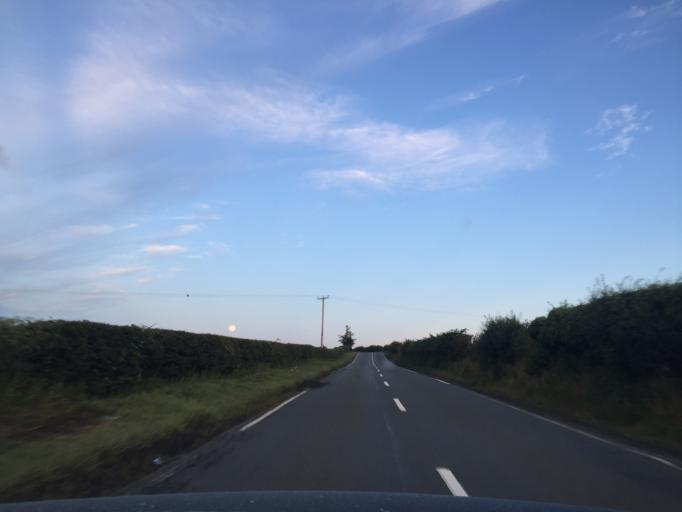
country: GB
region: Scotland
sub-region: The Scottish Borders
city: Duns
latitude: 55.7799
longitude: -2.3255
